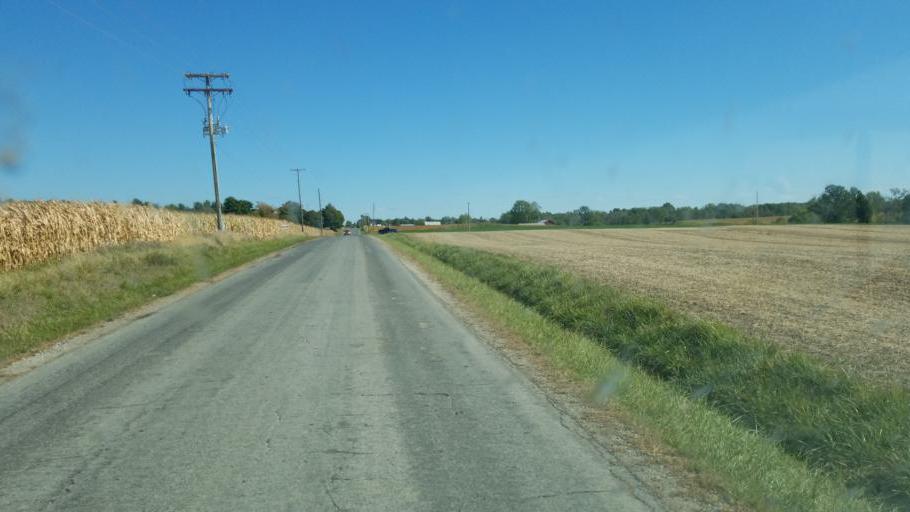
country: US
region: Ohio
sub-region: Huron County
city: Greenwich
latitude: 40.9932
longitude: -82.5101
